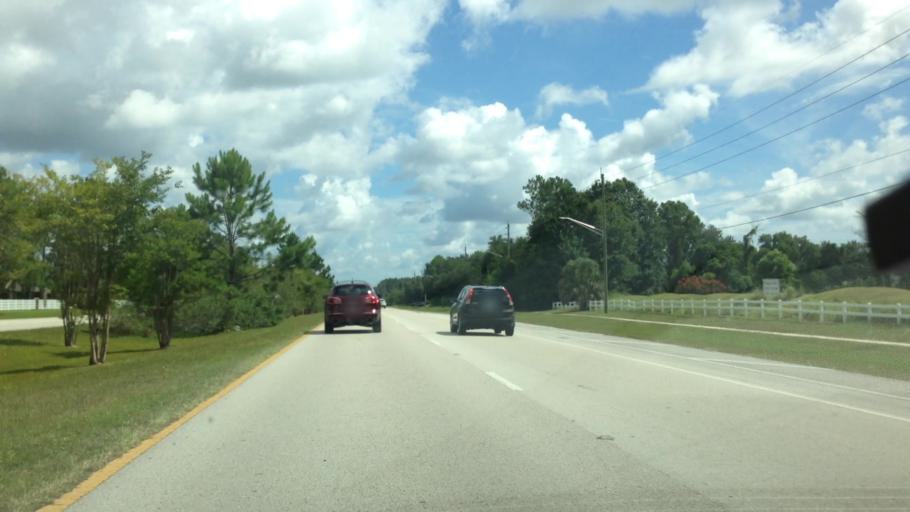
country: US
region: Florida
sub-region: Duval County
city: Jacksonville Beach
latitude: 30.2720
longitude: -81.4631
